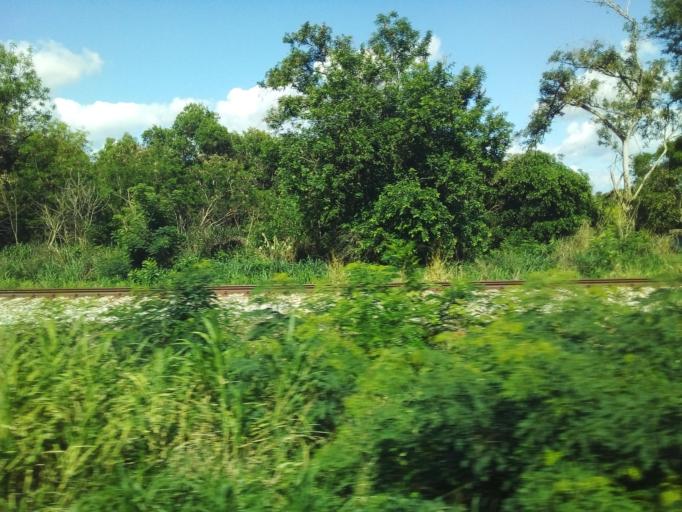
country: BR
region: Minas Gerais
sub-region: Governador Valadares
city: Governador Valadares
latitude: -18.8585
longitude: -41.8632
